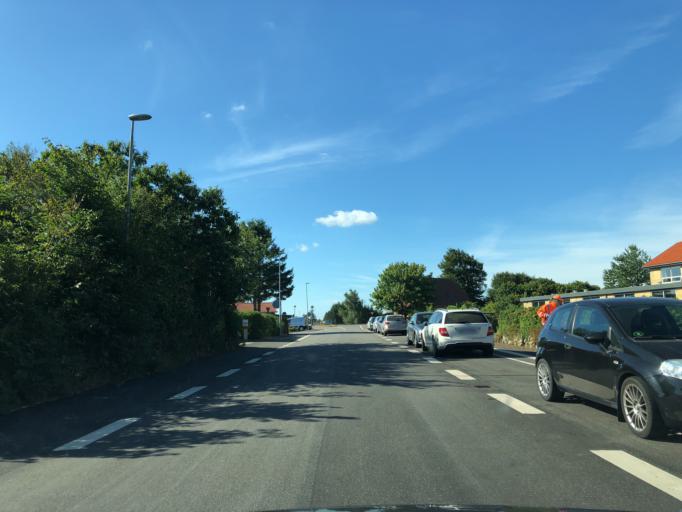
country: DK
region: Central Jutland
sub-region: Silkeborg Kommune
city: Silkeborg
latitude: 56.1485
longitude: 9.4627
